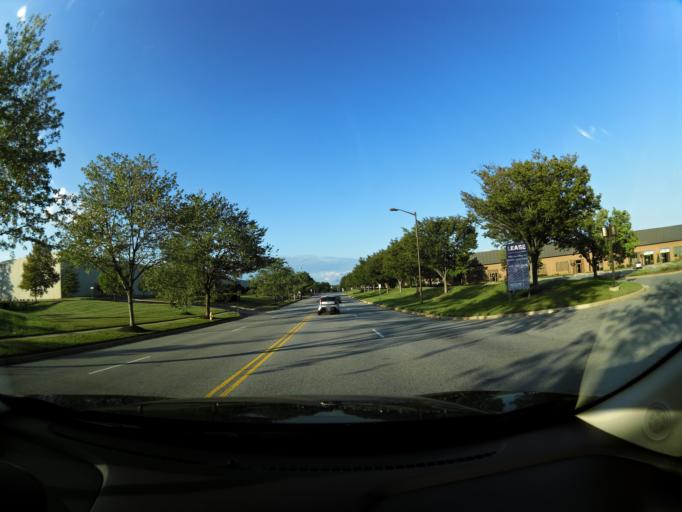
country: US
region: Maryland
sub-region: Howard County
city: Hanover
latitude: 39.1691
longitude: -76.7058
